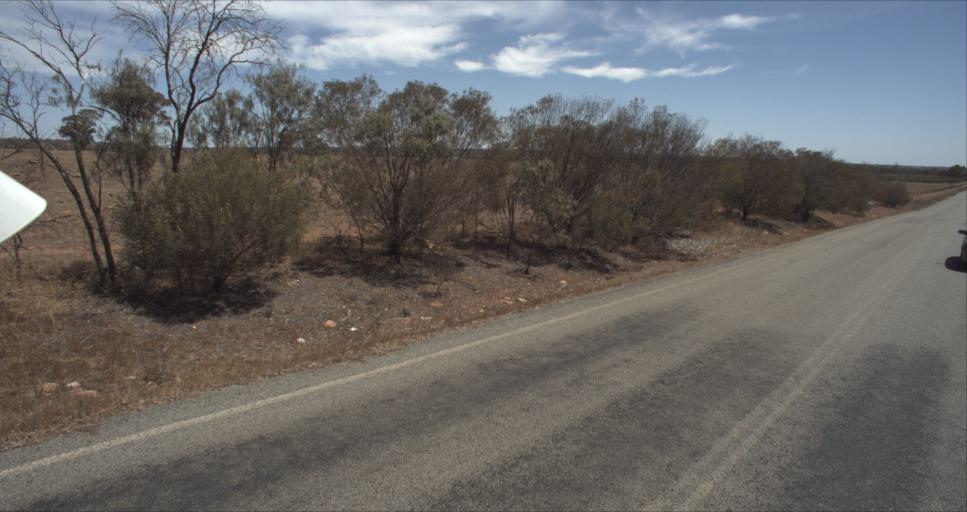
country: AU
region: New South Wales
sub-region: Leeton
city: Leeton
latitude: -34.5894
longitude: 146.4485
